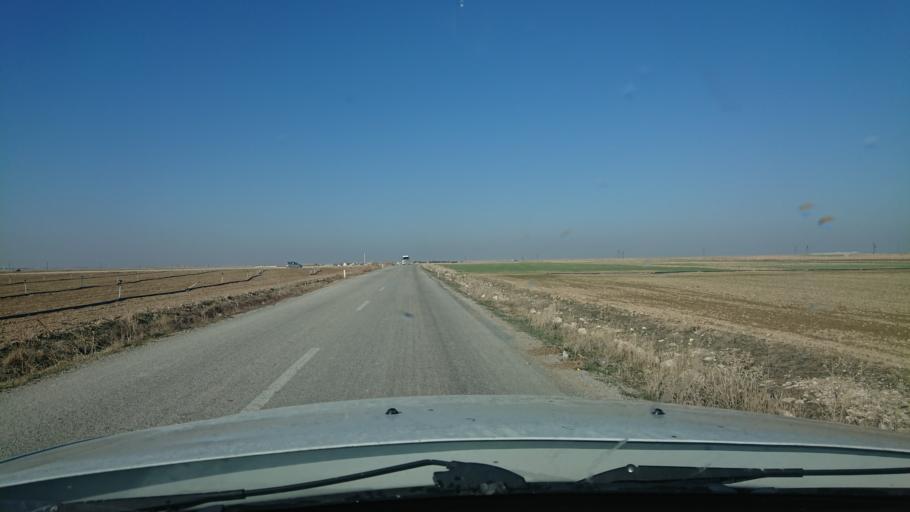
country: TR
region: Aksaray
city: Sultanhani
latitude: 38.2983
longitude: 33.5114
